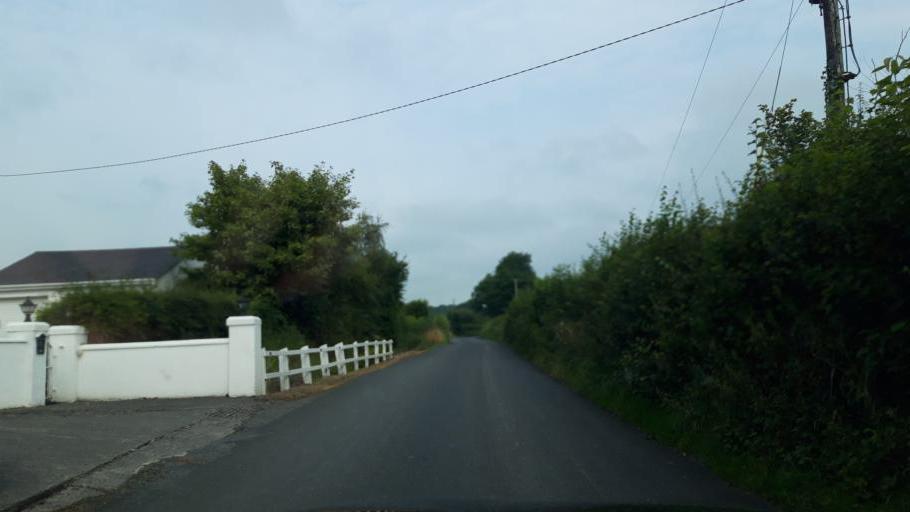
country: IE
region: Munster
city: Fethard
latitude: 52.5806
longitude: -7.5878
